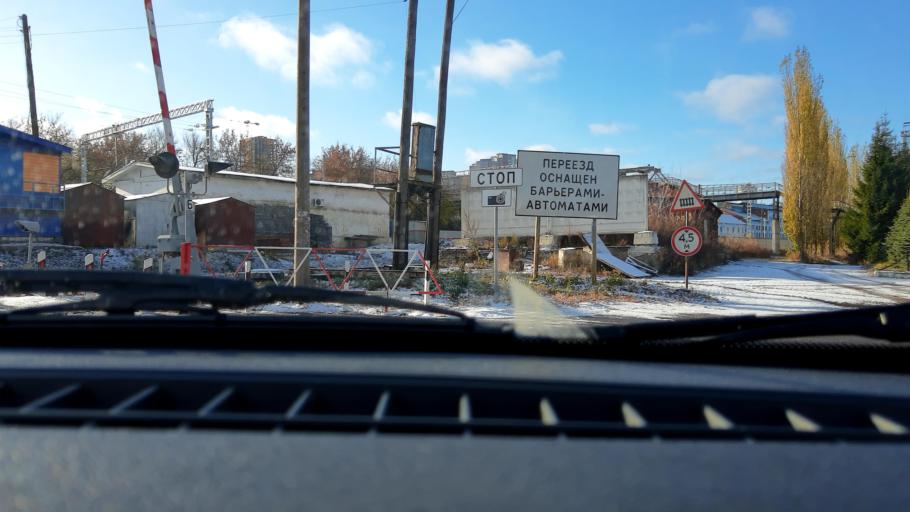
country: RU
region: Bashkortostan
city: Ufa
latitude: 54.7541
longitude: 55.9629
